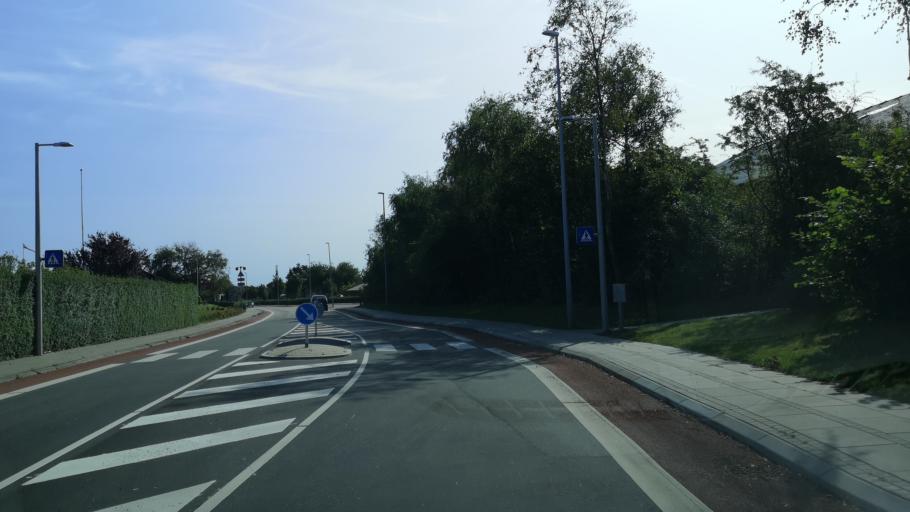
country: DK
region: Central Jutland
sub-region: Ringkobing-Skjern Kommune
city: Videbaek
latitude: 56.0867
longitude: 8.6197
